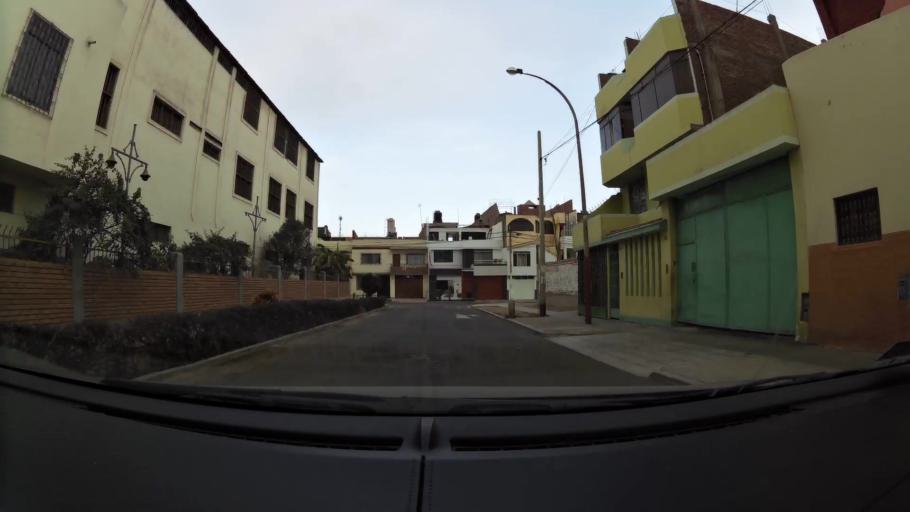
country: PE
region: La Libertad
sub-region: Provincia de Trujillo
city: Trujillo
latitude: -8.0990
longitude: -79.0291
